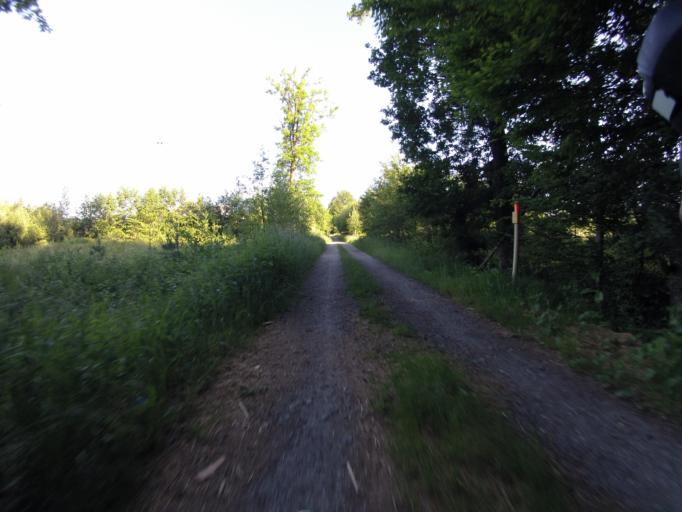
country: DE
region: Lower Saxony
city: Bad Bentheim
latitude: 52.3130
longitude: 7.1341
